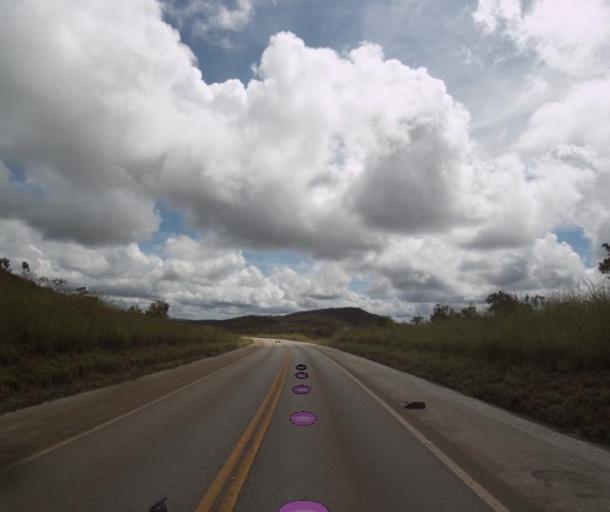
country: BR
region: Goias
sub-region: Pirenopolis
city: Pirenopolis
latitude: -15.7546
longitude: -48.5844
